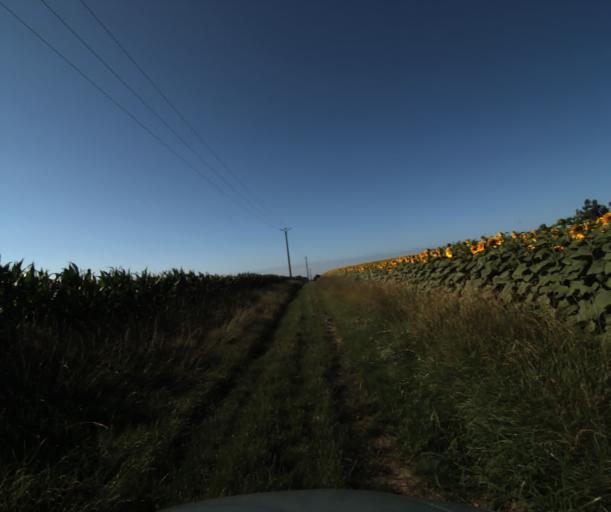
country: FR
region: Midi-Pyrenees
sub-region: Departement de la Haute-Garonne
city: Labarthe-sur-Leze
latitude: 43.4438
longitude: 1.3765
